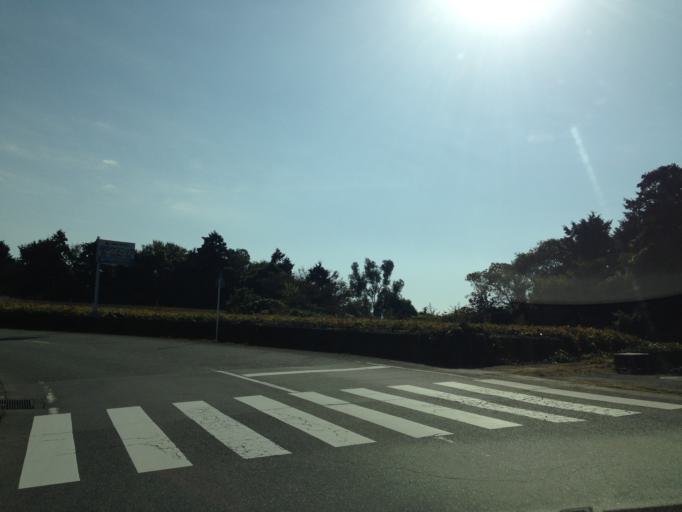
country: JP
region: Shizuoka
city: Mishima
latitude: 35.1586
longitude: 138.9355
